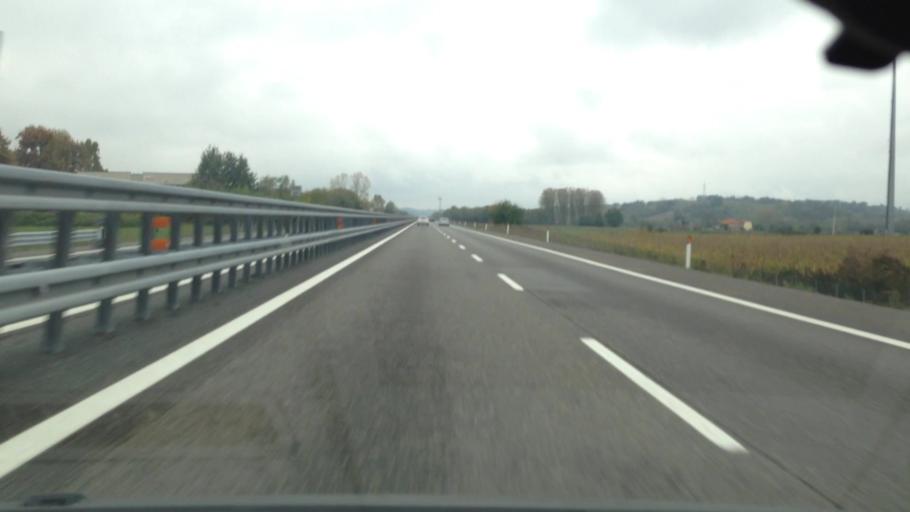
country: IT
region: Piedmont
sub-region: Provincia di Asti
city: Villafranca d'Asti
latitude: 44.9161
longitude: 8.0350
